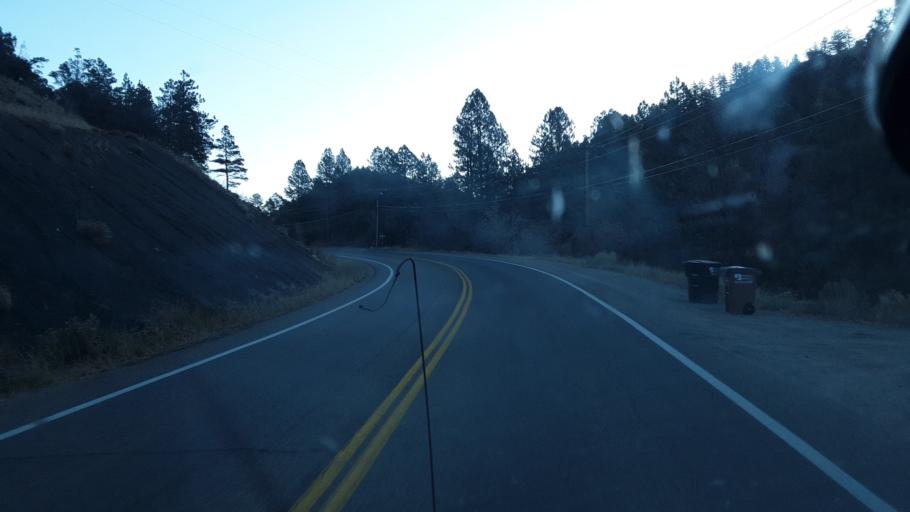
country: US
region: Colorado
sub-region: La Plata County
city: Durango
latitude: 37.3070
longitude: -107.8195
